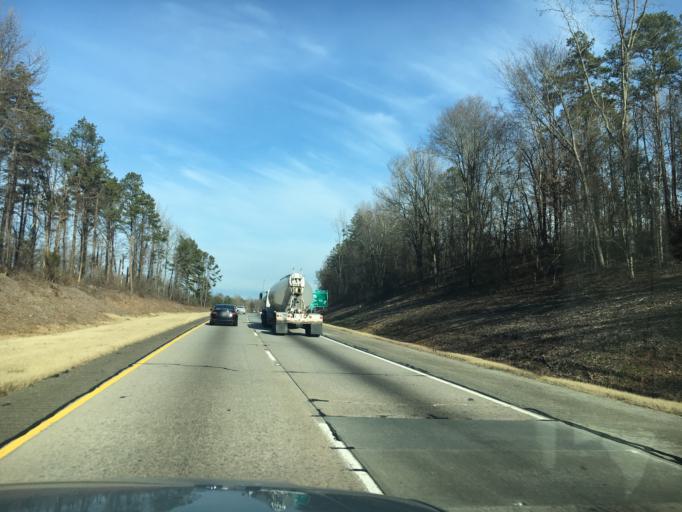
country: US
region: Georgia
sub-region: Banks County
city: Homer
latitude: 34.2942
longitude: -83.4134
